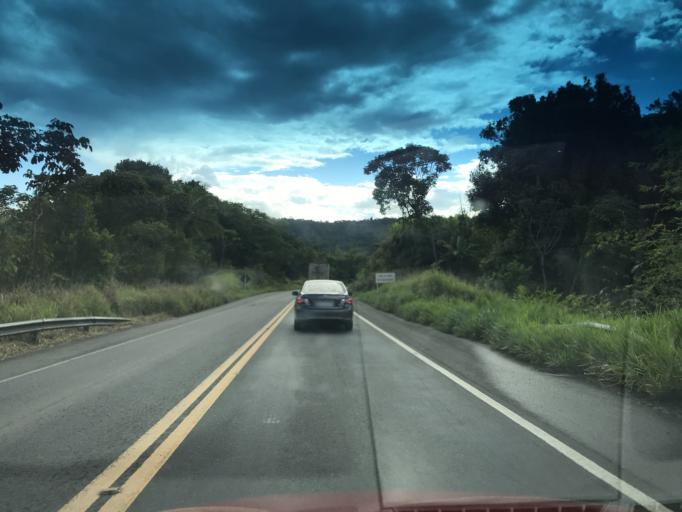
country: BR
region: Bahia
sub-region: Ibirapitanga
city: Ibirapitanga
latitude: -14.1715
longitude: -39.3244
